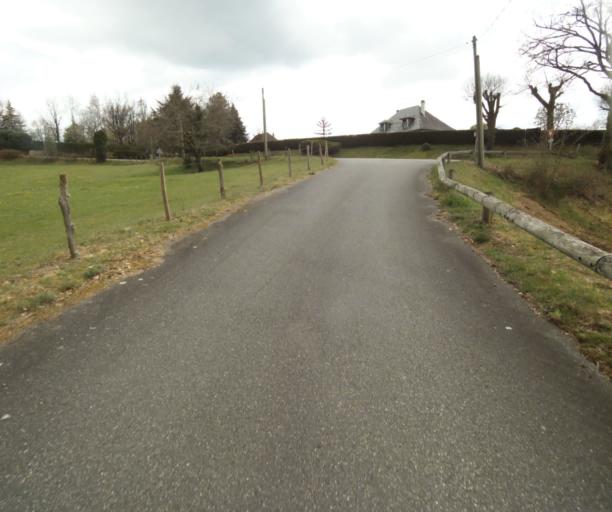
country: FR
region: Limousin
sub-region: Departement de la Correze
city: Naves
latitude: 45.3084
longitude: 1.8118
